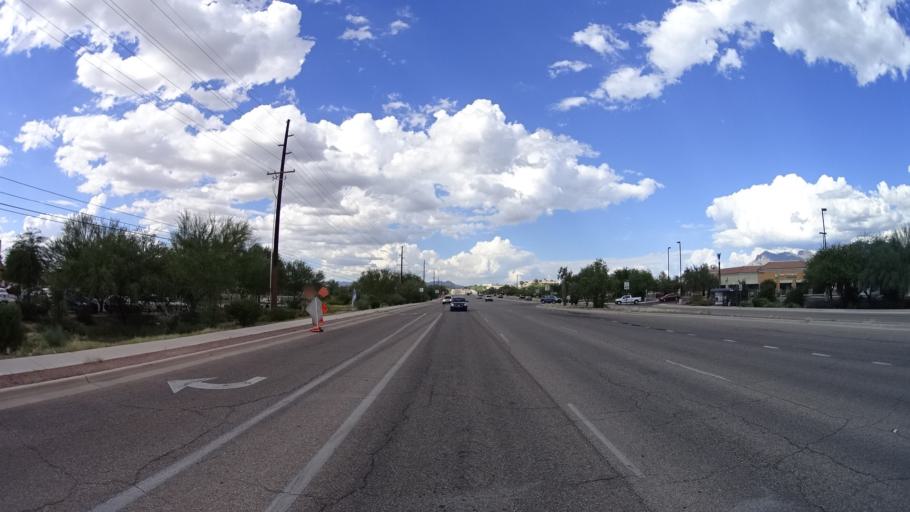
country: US
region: Arizona
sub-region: Pima County
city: Flowing Wells
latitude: 32.3061
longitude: -111.0121
